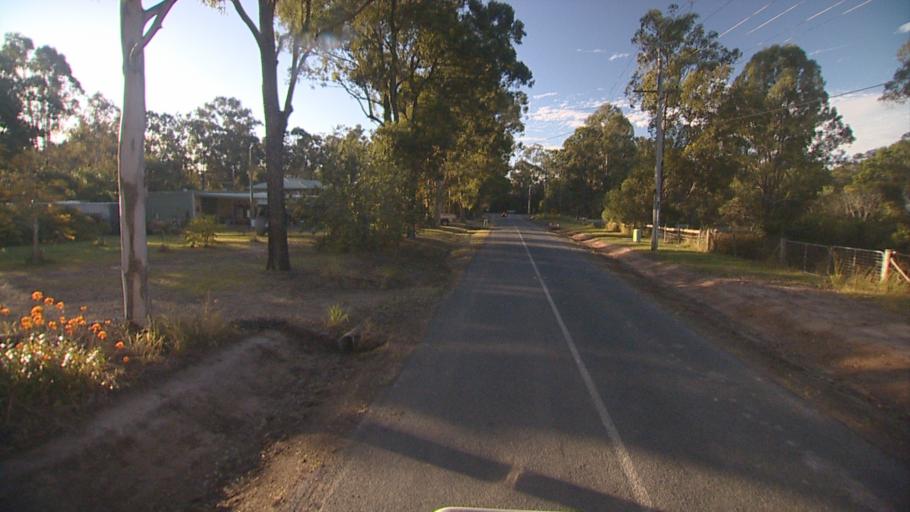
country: AU
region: Queensland
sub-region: Logan
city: Waterford West
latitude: -27.7208
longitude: 153.1482
